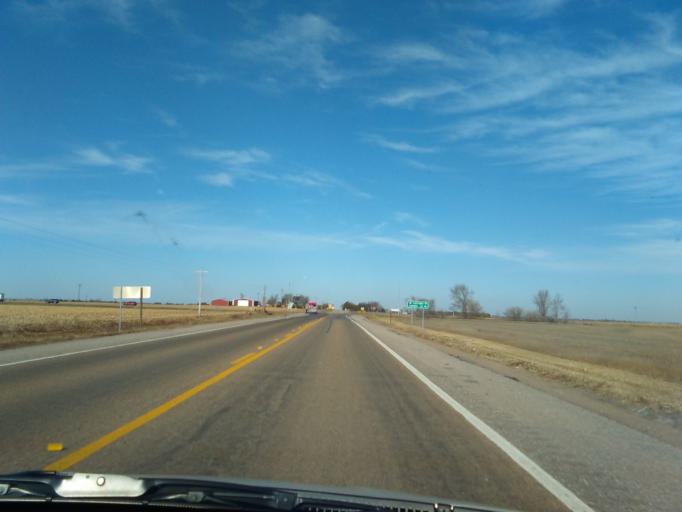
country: US
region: Nebraska
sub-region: Clay County
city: Clay Center
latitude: 40.5804
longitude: -98.0516
